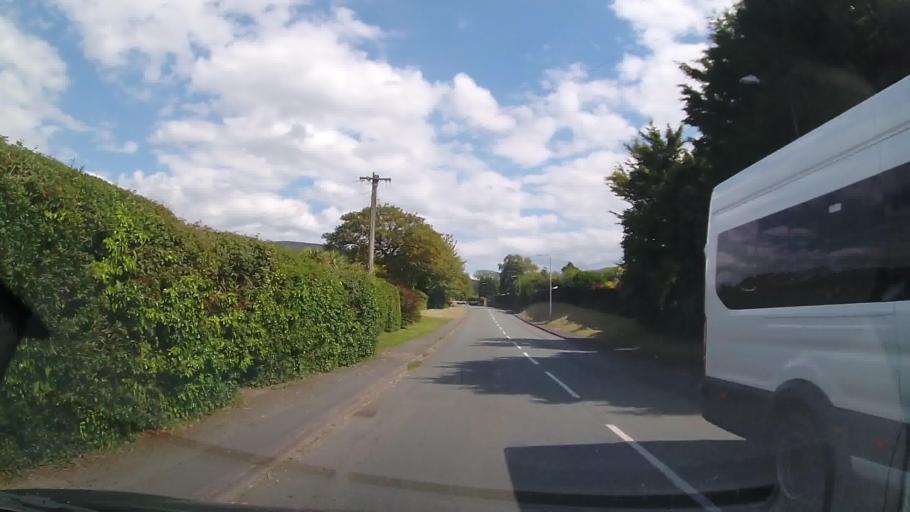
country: GB
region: Wales
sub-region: Gwynedd
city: Tywyn
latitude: 52.6061
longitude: -4.0552
